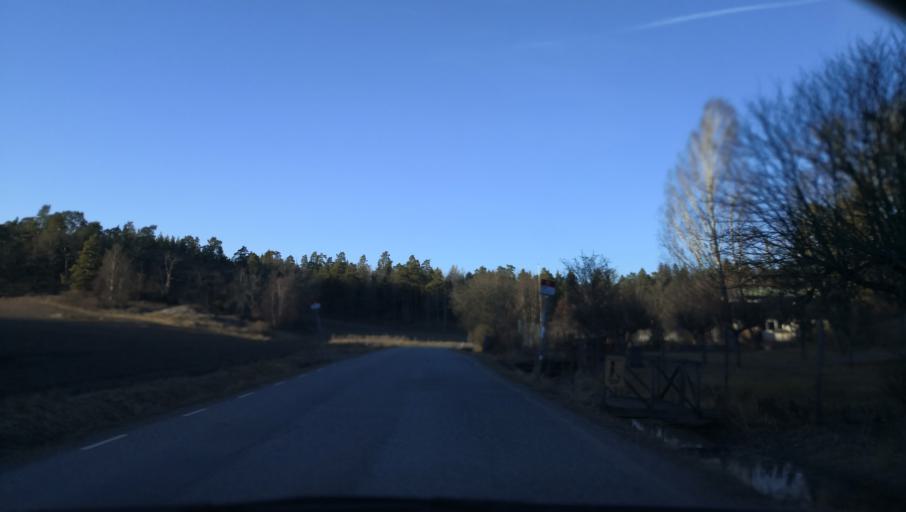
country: SE
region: Stockholm
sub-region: Varmdo Kommun
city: Mortnas
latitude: 59.3310
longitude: 18.4265
